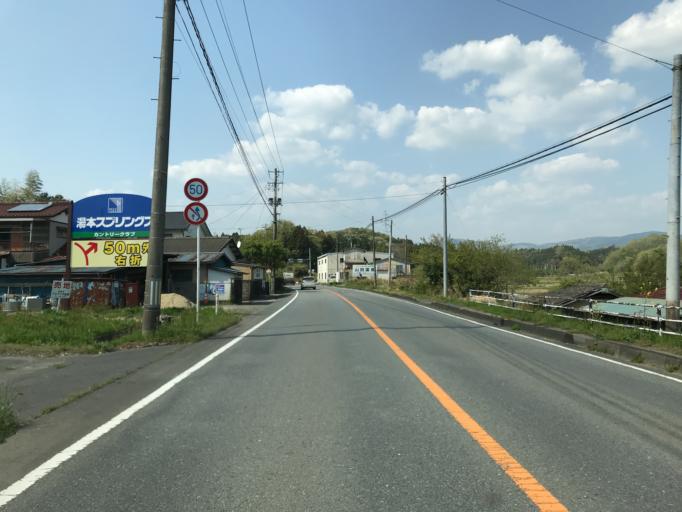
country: JP
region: Fukushima
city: Iwaki
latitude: 36.9596
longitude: 140.7543
